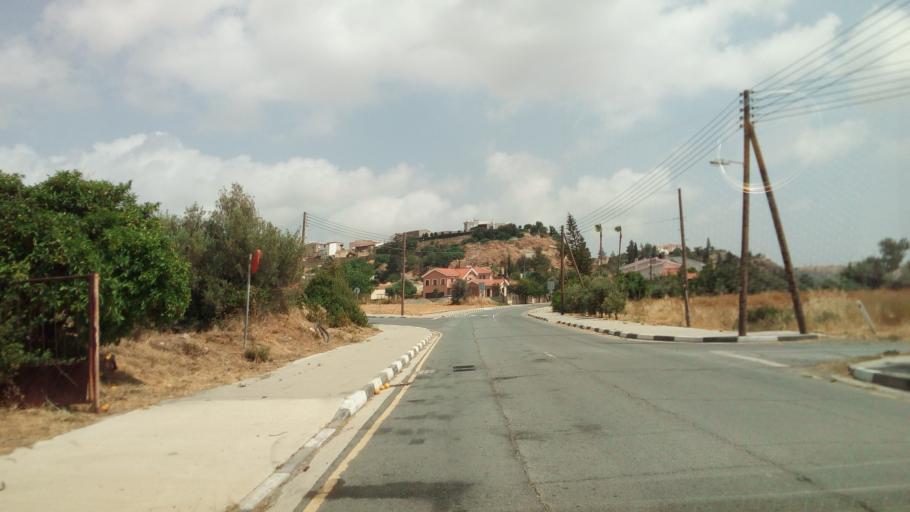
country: CY
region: Larnaka
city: Kofinou
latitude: 34.8011
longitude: 33.3305
